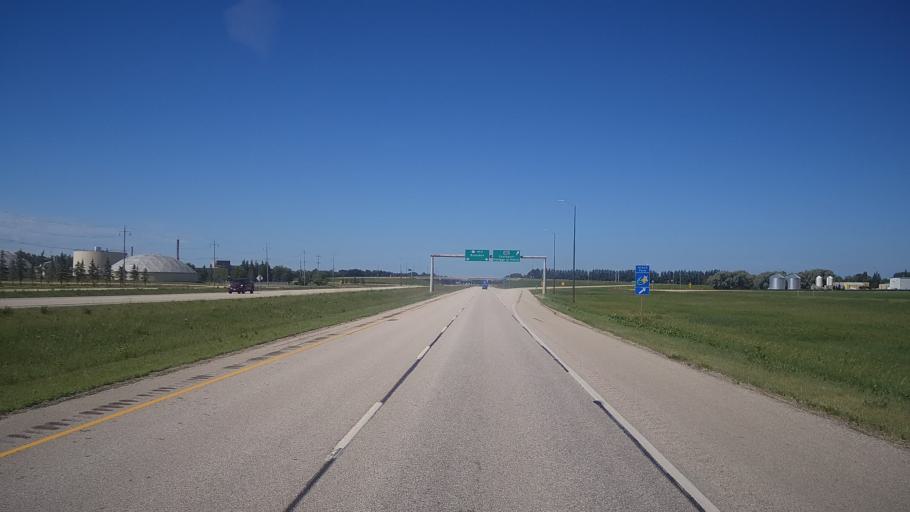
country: CA
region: Manitoba
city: Portage la Prairie
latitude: 49.9577
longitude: -98.2653
